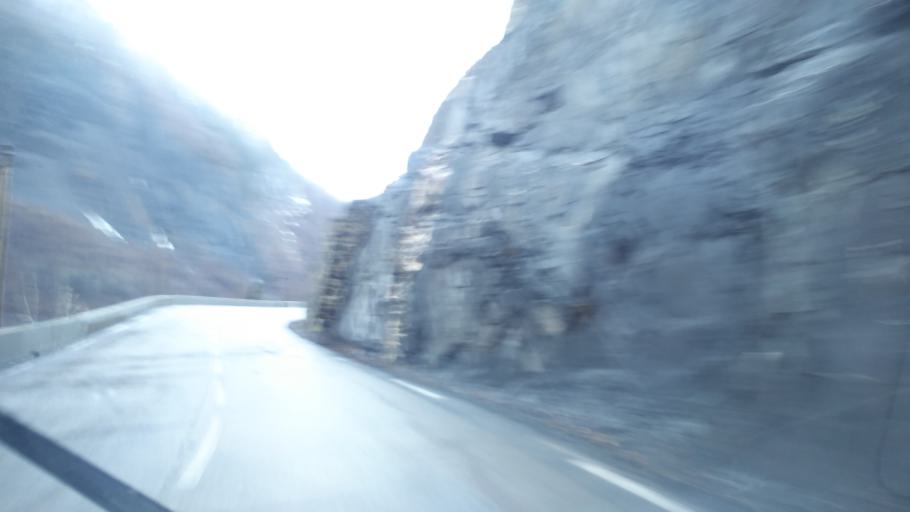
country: FR
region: Rhone-Alpes
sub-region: Departement de l'Isere
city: Mont-de-Lans
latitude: 45.0443
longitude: 6.1618
